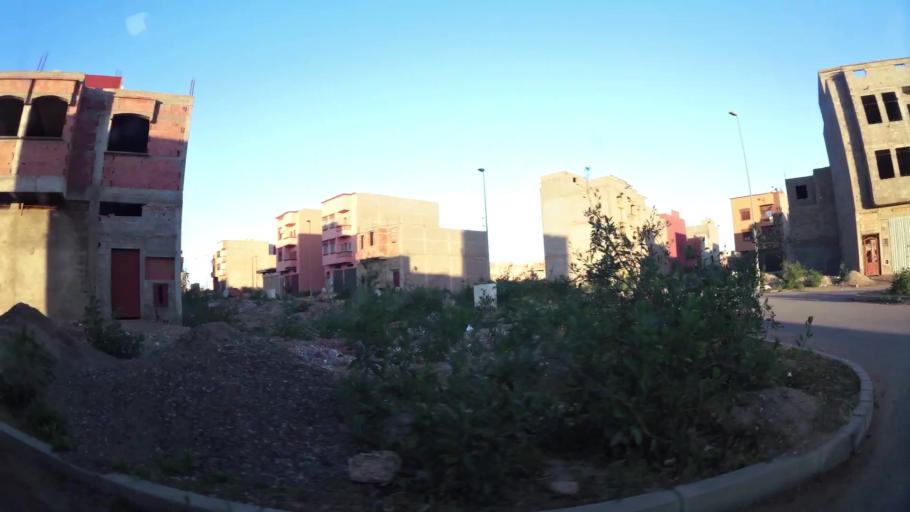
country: MA
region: Marrakech-Tensift-Al Haouz
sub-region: Kelaa-Des-Sraghna
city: Sidi Abdallah
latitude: 32.2394
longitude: -7.9421
